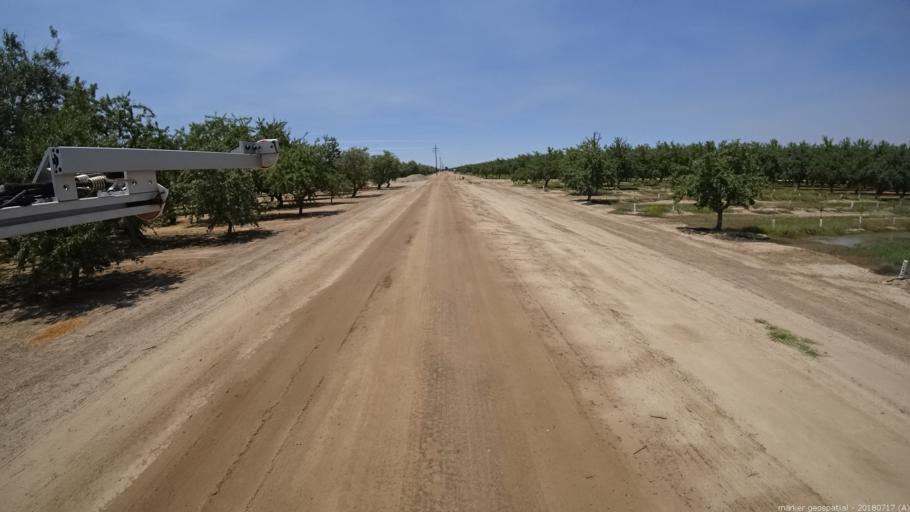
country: US
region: California
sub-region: Madera County
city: Fairmead
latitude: 37.1195
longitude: -120.1327
